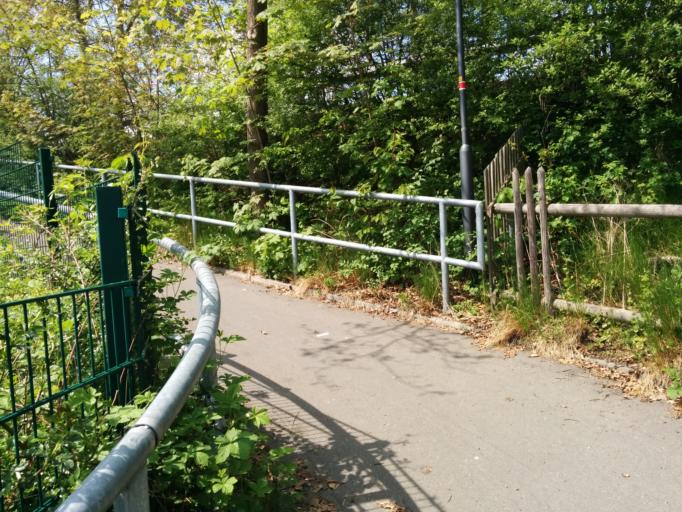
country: DE
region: Saxony
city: Floha
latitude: 50.8432
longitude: 13.0776
